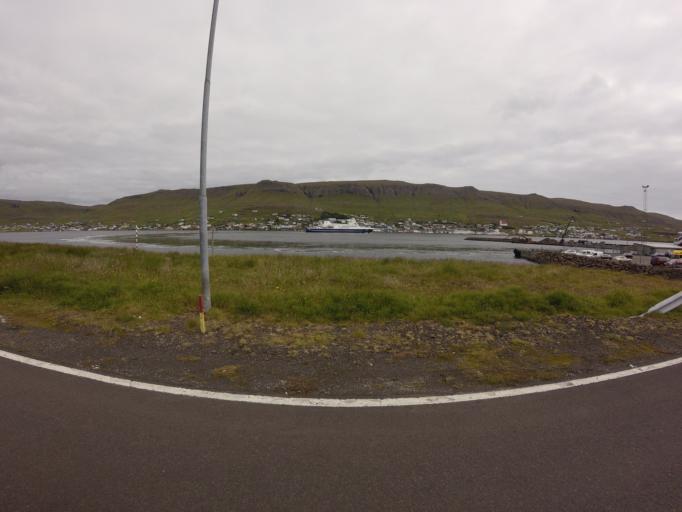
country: FO
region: Suduroy
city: Tvoroyri
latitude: 61.5484
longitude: -6.8209
